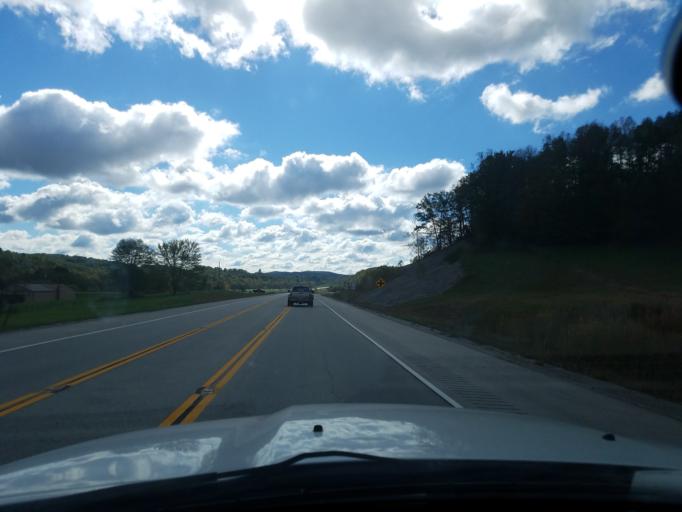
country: US
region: Kentucky
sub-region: Rockcastle County
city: Brodhead
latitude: 37.3926
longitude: -84.4242
